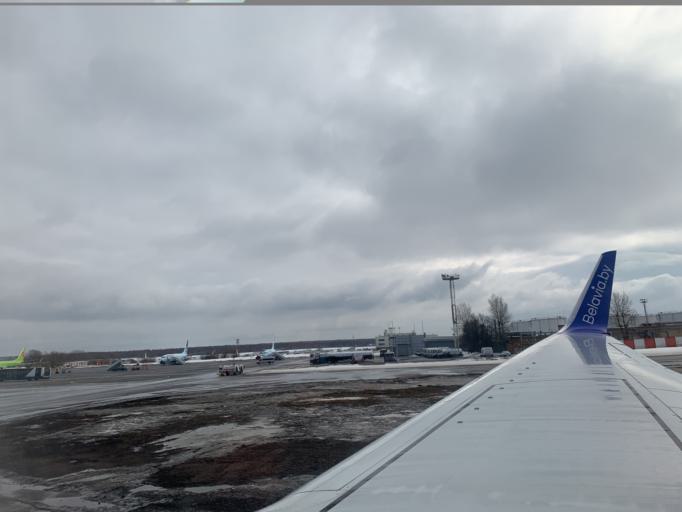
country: RU
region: Moskovskaya
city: Yakovlevskoye
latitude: 55.4100
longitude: 37.8990
